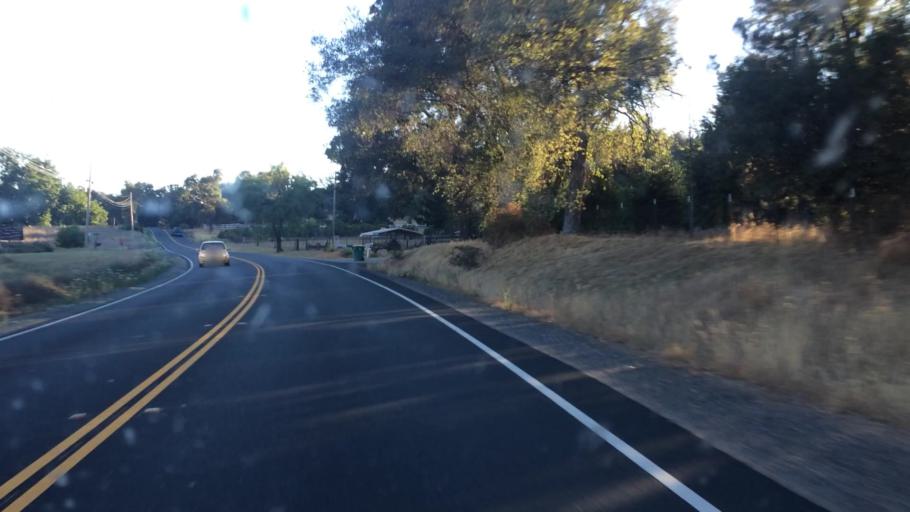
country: US
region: California
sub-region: El Dorado County
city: Deer Park
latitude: 38.6666
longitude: -120.8528
